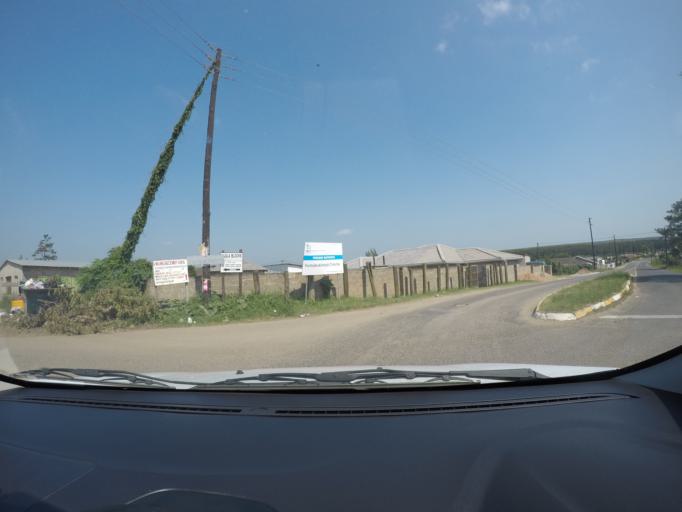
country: ZA
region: KwaZulu-Natal
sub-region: uThungulu District Municipality
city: eSikhawini
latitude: -28.8927
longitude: 31.8810
